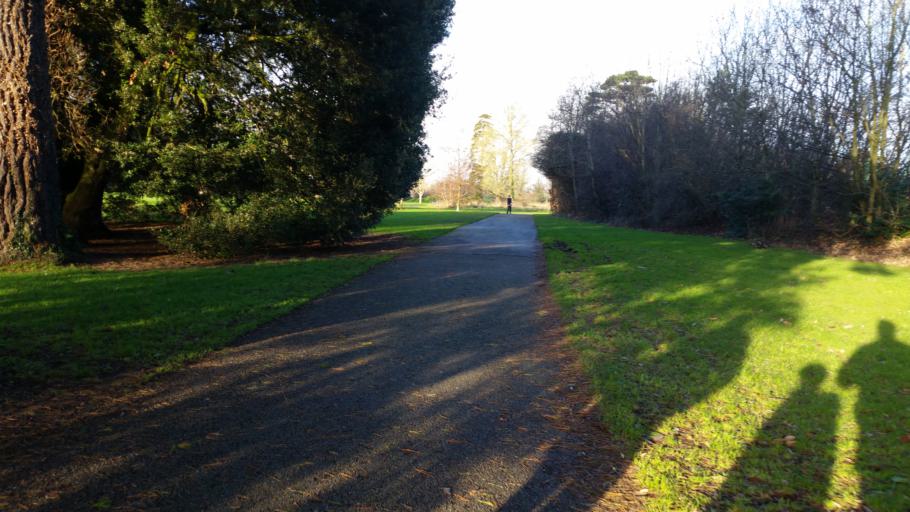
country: IE
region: Leinster
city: Beaumont
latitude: 53.3994
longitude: -6.2465
